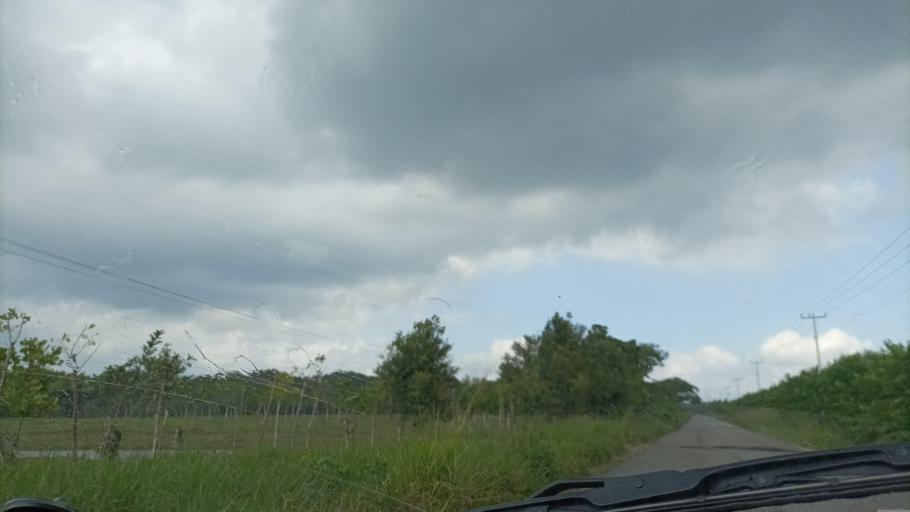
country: MX
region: Veracruz
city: Las Choapas
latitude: 17.8357
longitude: -94.1047
